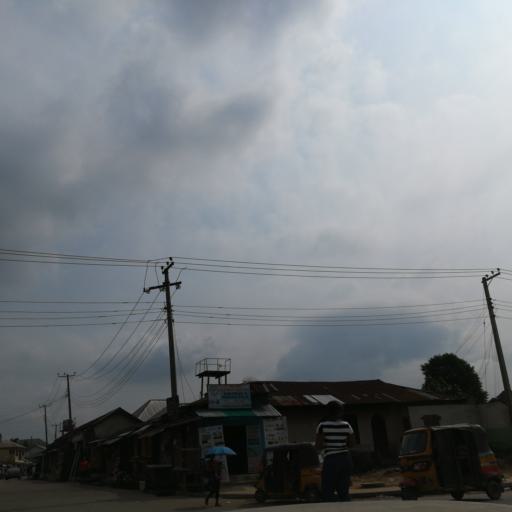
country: NG
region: Rivers
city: Port Harcourt
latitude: 4.8386
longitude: 7.0700
